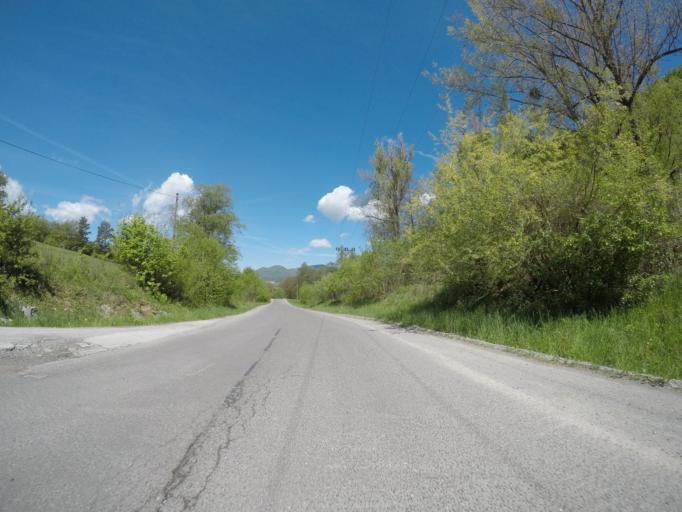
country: SK
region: Banskobystricky
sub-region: Okres Banska Bystrica
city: Banska Bystrica
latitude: 48.7316
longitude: 19.2051
